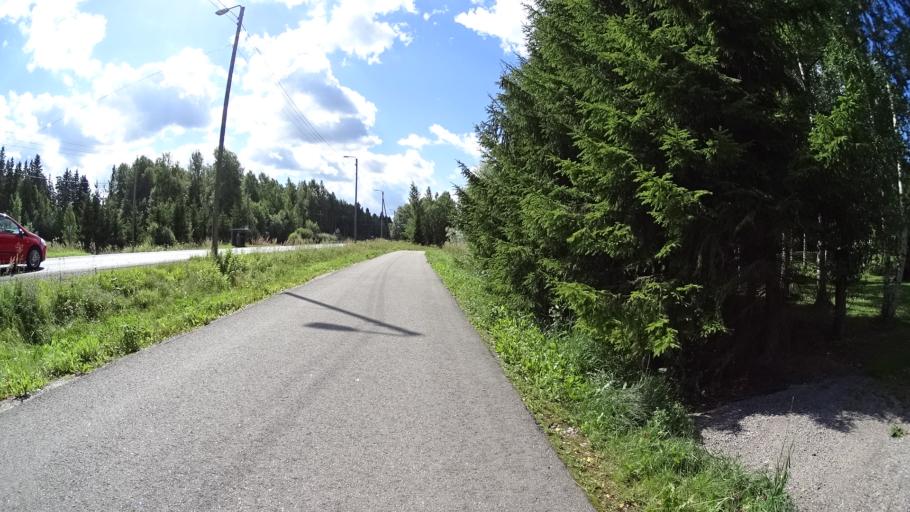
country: FI
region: Uusimaa
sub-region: Helsinki
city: Tuusula
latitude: 60.4258
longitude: 25.0535
